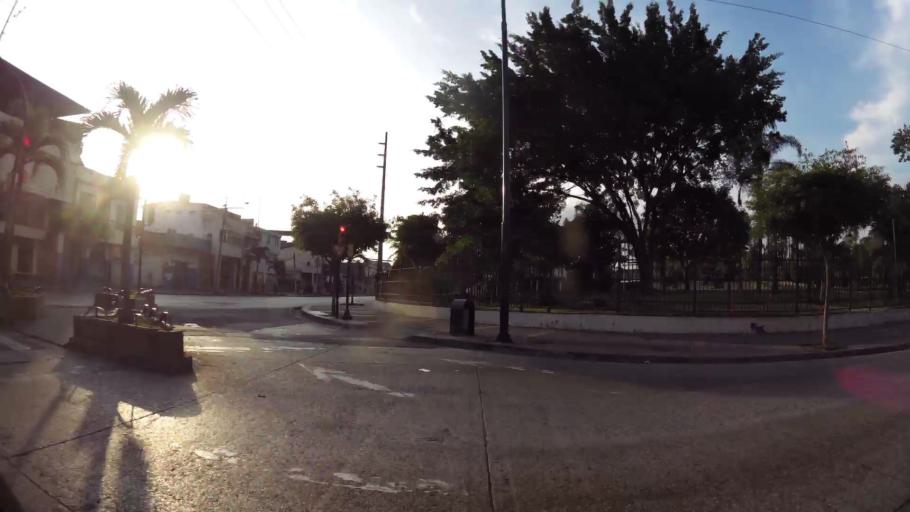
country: EC
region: Guayas
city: Guayaquil
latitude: -2.2085
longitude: -79.8951
